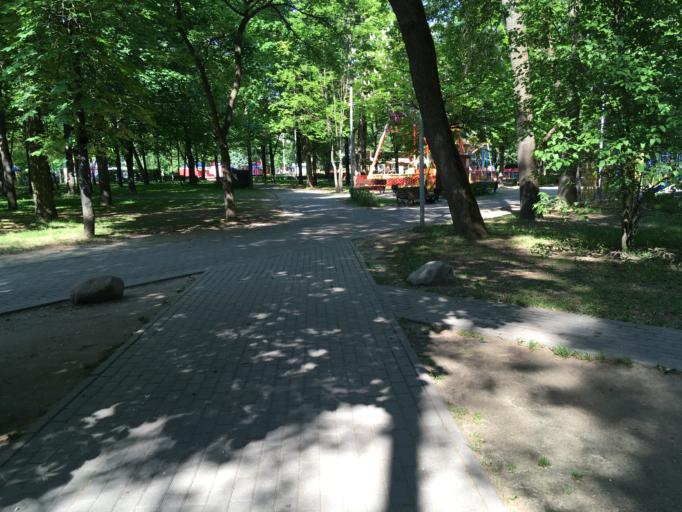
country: BY
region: Minsk
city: Minsk
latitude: 53.9195
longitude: 27.6167
